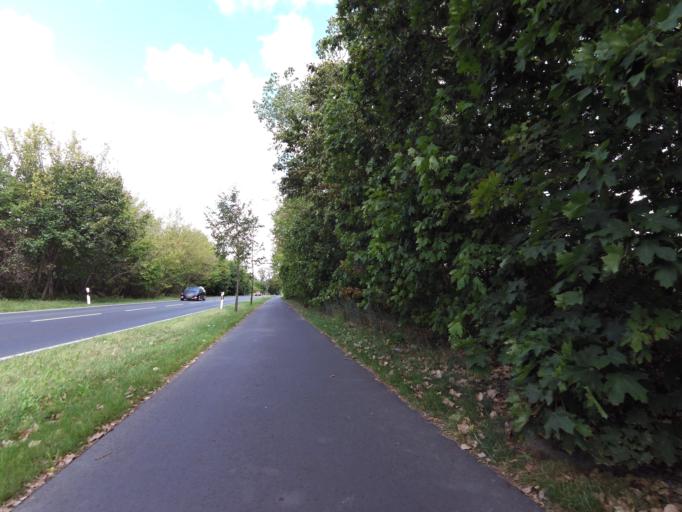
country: DE
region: Brandenburg
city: Grossbeeren
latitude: 52.3683
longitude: 13.3163
